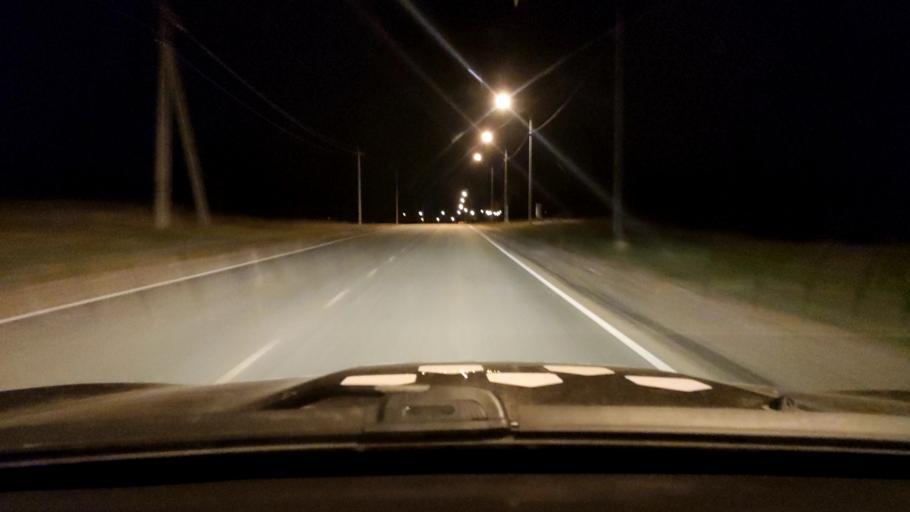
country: RU
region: Samara
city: Zhigulevsk
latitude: 53.4925
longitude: 49.5291
